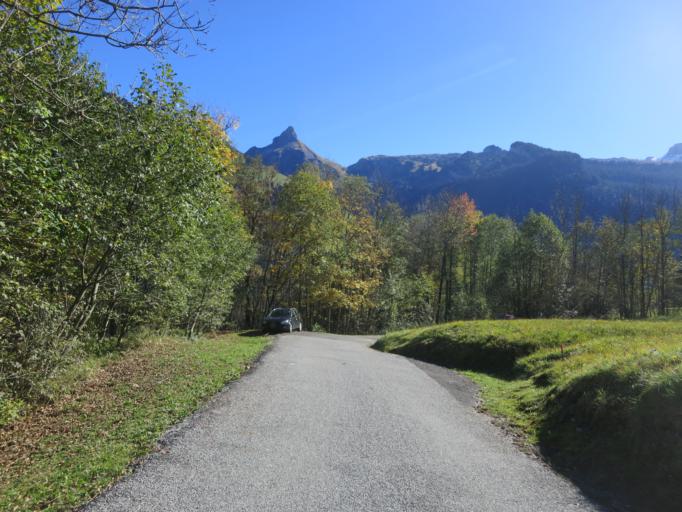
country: CH
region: Schwyz
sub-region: Bezirk March
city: Vorderthal
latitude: 47.0865
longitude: 8.9156
